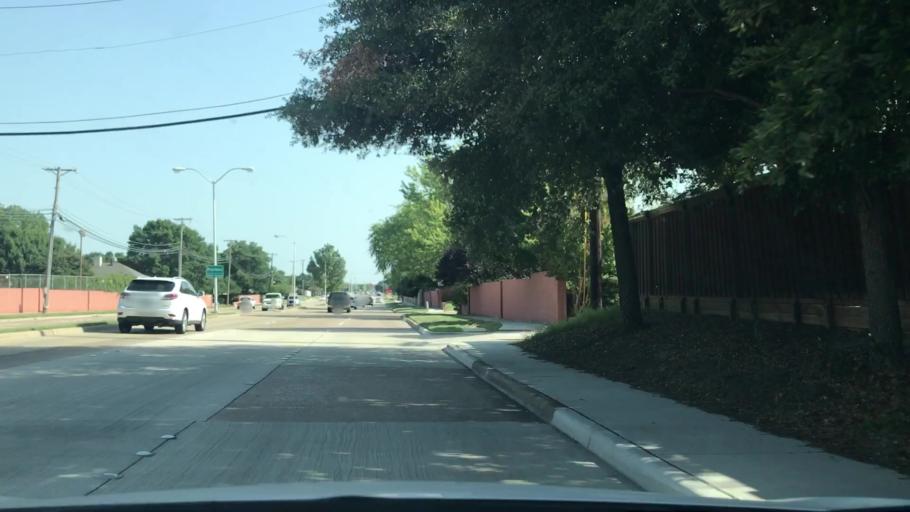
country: US
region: Texas
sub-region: Collin County
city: Plano
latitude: 33.0456
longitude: -96.7534
